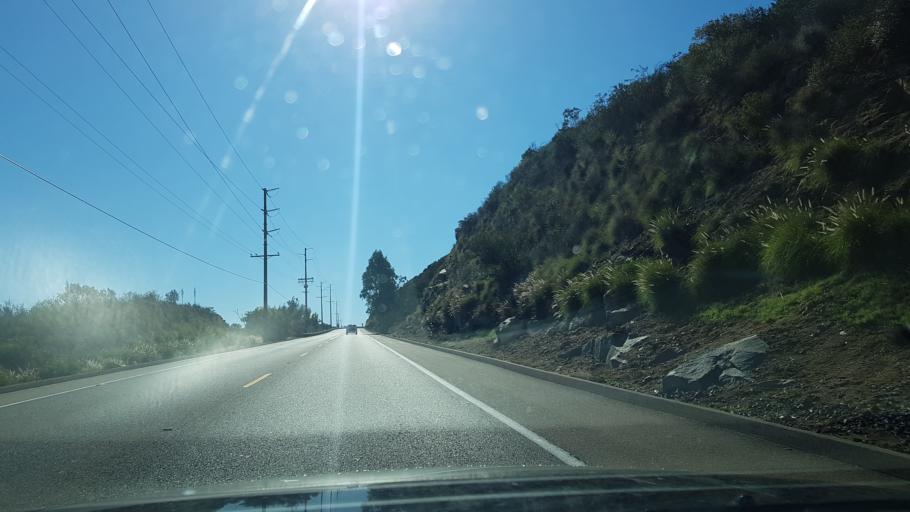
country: US
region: California
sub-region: San Diego County
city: Escondido
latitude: 33.0767
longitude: -117.1209
